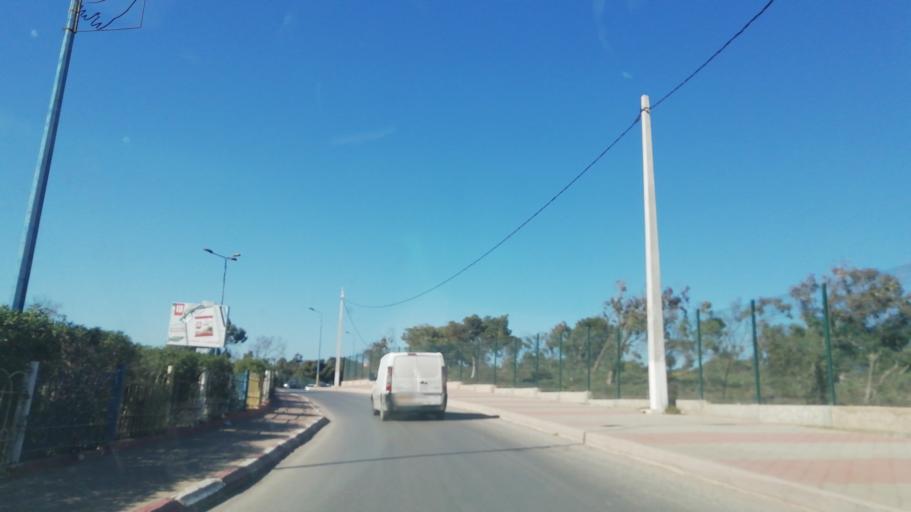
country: DZ
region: Oran
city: Bir el Djir
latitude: 35.7421
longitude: -0.5675
